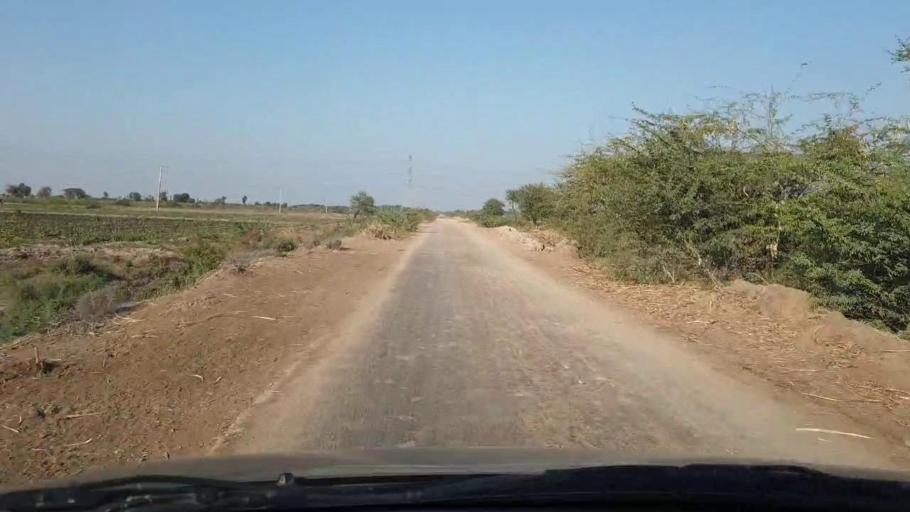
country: PK
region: Sindh
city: Samaro
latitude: 25.1486
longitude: 69.3080
